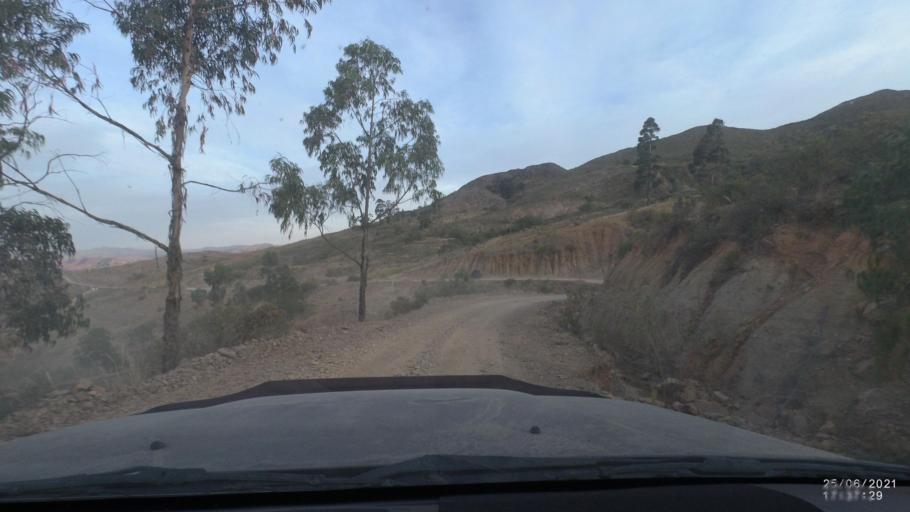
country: BO
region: Cochabamba
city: Mizque
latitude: -17.9577
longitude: -65.6462
